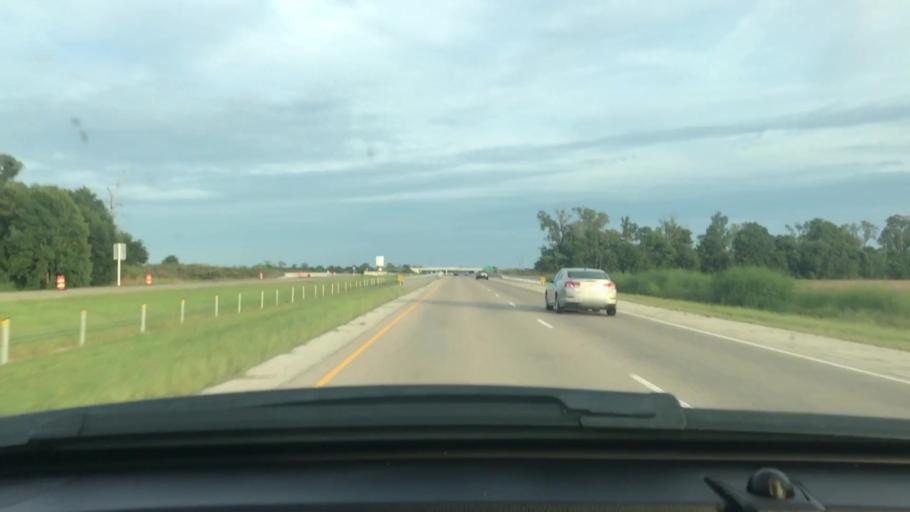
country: US
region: Arkansas
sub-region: Craighead County
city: Bay
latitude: 35.7803
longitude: -90.5942
